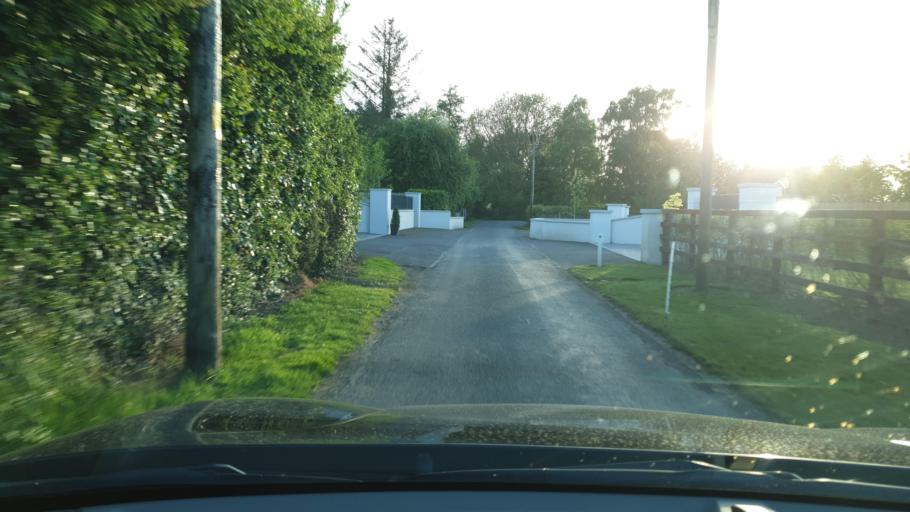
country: IE
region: Leinster
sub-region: An Mhi
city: Ashbourne
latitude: 53.4801
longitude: -6.4031
